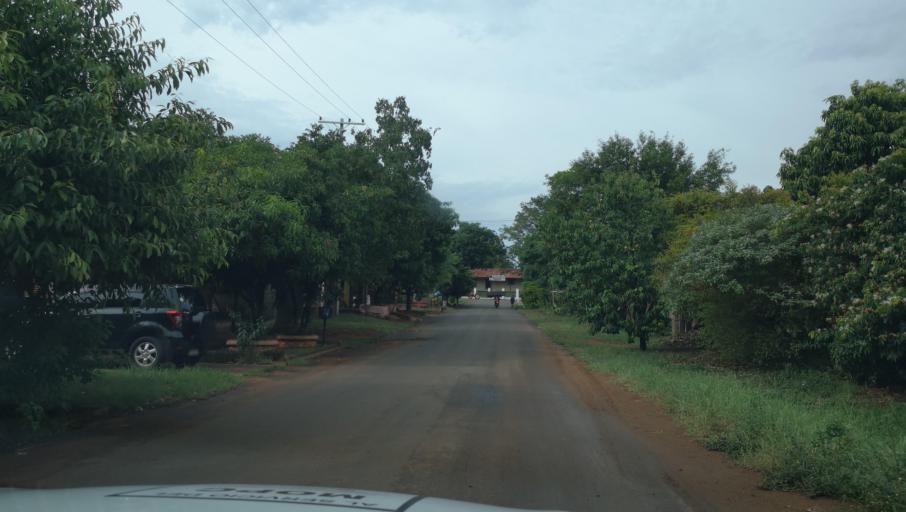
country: PY
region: Misiones
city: Santa Maria
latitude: -26.8876
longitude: -57.0335
